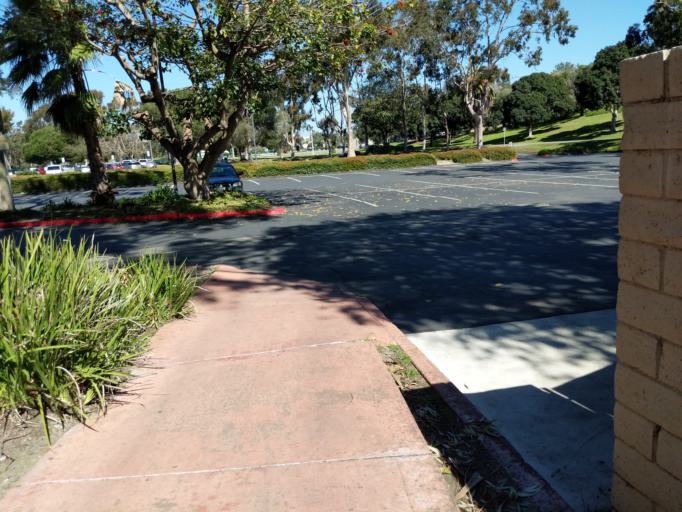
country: US
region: California
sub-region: San Diego County
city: San Diego
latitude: 32.7604
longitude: -117.2337
